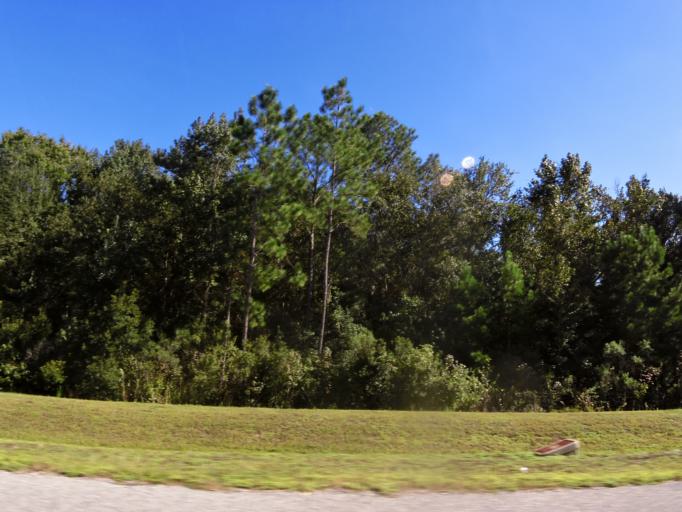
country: US
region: Florida
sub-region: Saint Johns County
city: Palm Valley
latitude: 30.0980
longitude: -81.4673
